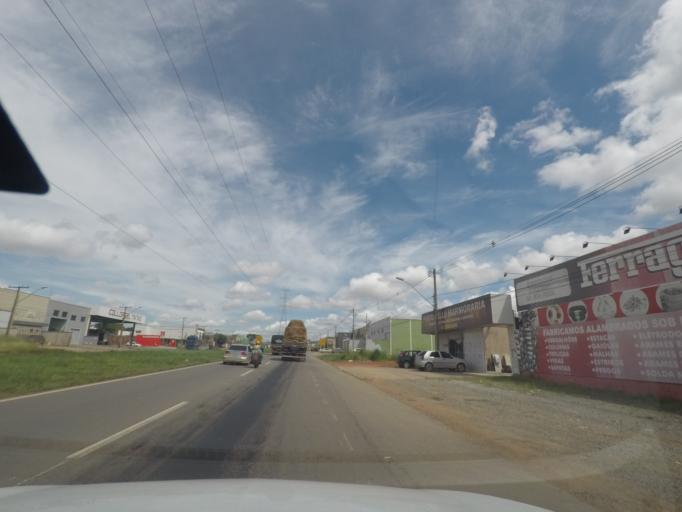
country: BR
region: Goias
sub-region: Goiania
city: Goiania
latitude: -16.7408
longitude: -49.3455
